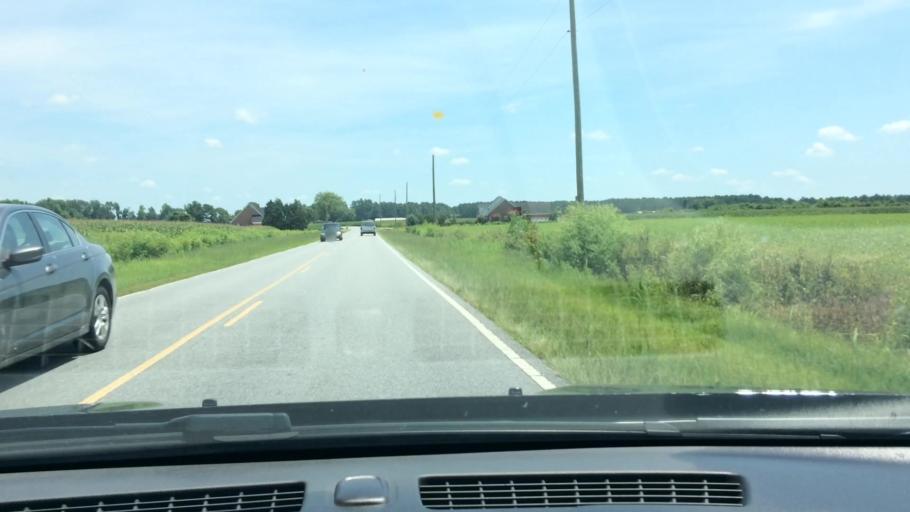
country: US
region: North Carolina
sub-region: Pitt County
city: Windsor
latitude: 35.5374
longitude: -77.3018
